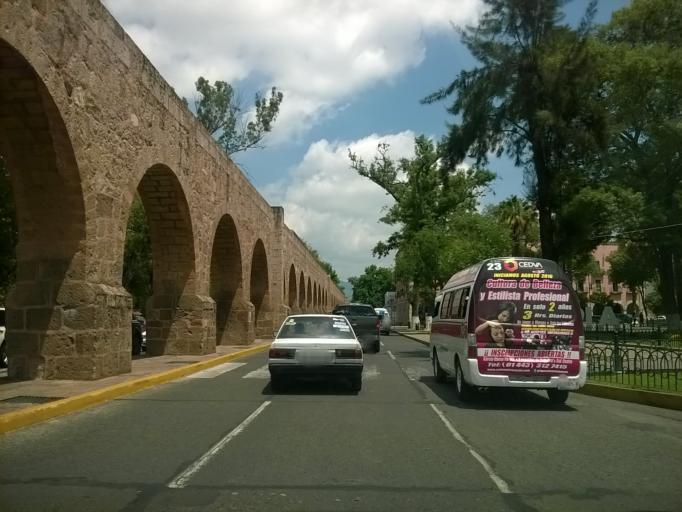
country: MX
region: Michoacan
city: Morelia
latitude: 19.6992
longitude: -101.1782
